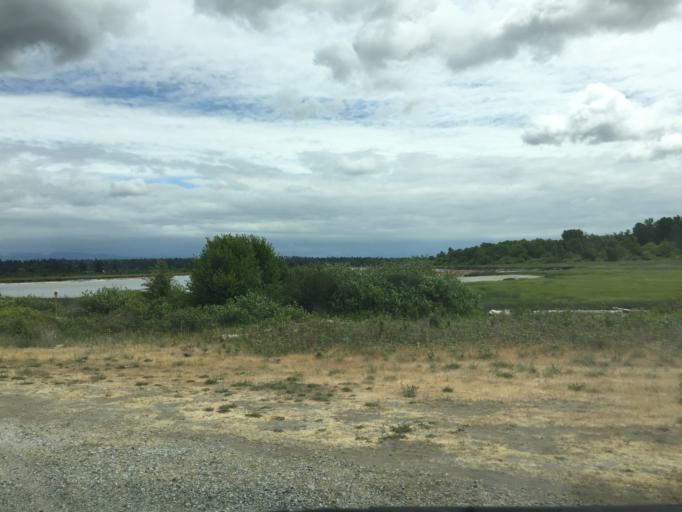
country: CA
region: British Columbia
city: Richmond
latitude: 49.2109
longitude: -123.2027
